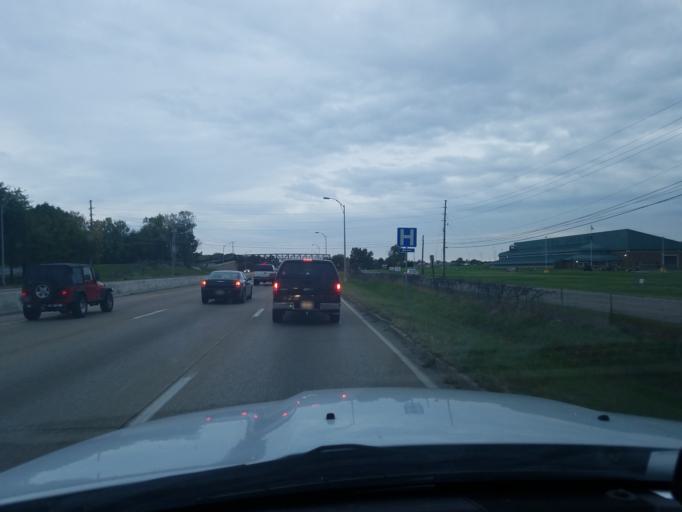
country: US
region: Indiana
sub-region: Vanderburgh County
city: Evansville
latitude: 37.9769
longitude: -87.5066
